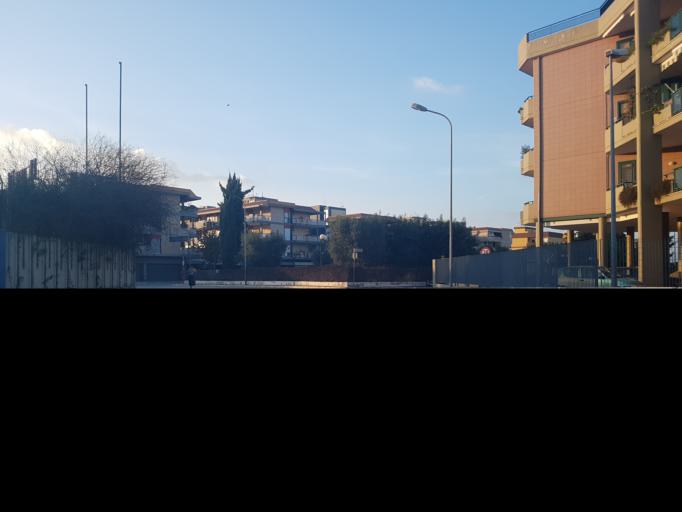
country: IT
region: Apulia
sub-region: Provincia di Bari
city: Bitritto
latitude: 41.0479
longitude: 16.8255
